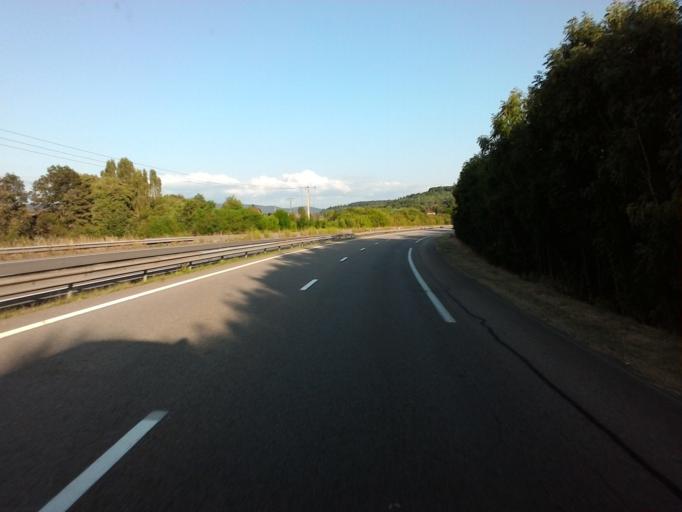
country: FR
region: Lorraine
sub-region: Departement des Vosges
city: Arches
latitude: 48.1216
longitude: 6.5318
